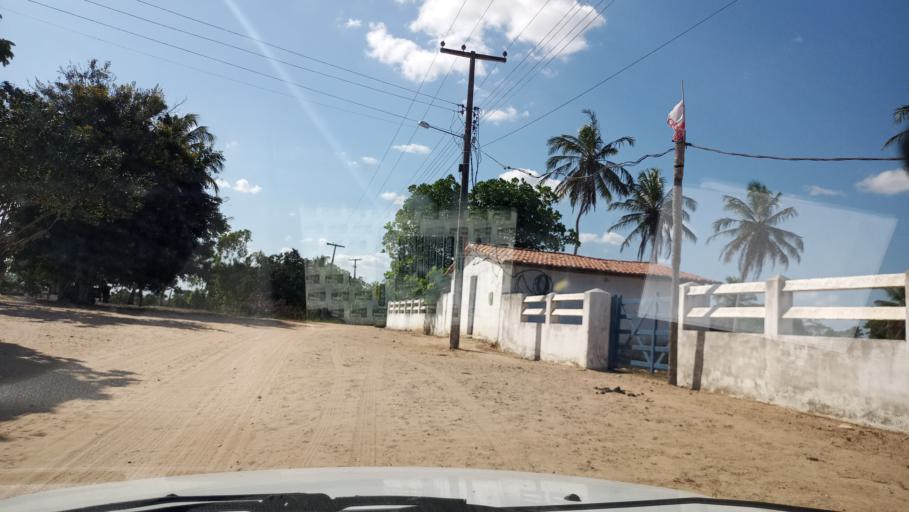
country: BR
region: Rio Grande do Norte
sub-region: Brejinho
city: Brejinho
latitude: -6.1719
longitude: -35.4696
